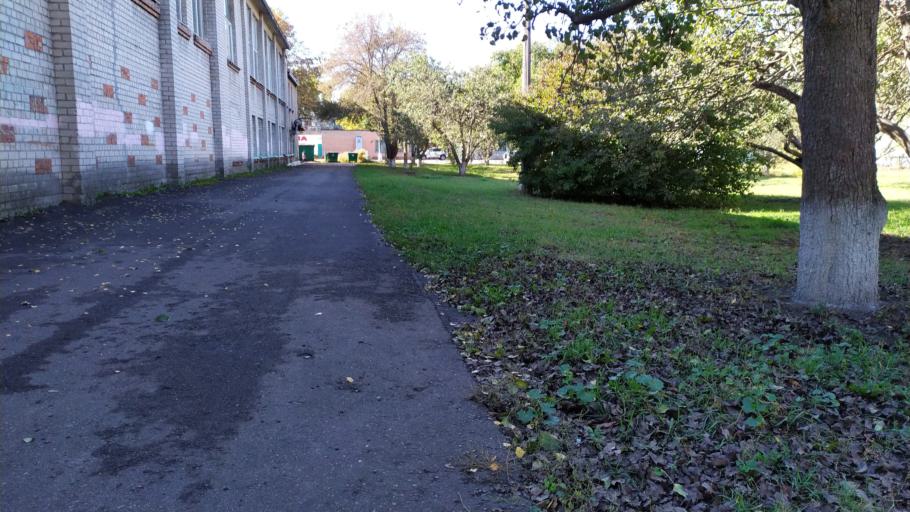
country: RU
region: Kursk
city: Kursk
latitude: 51.6501
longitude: 36.1420
